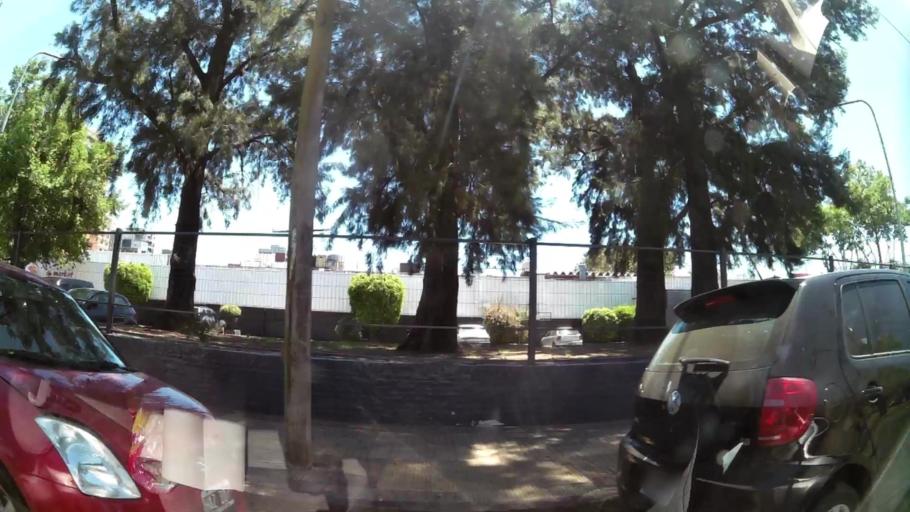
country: AR
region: Buenos Aires
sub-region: Partido de Tigre
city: Tigre
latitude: -34.4419
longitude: -58.5530
